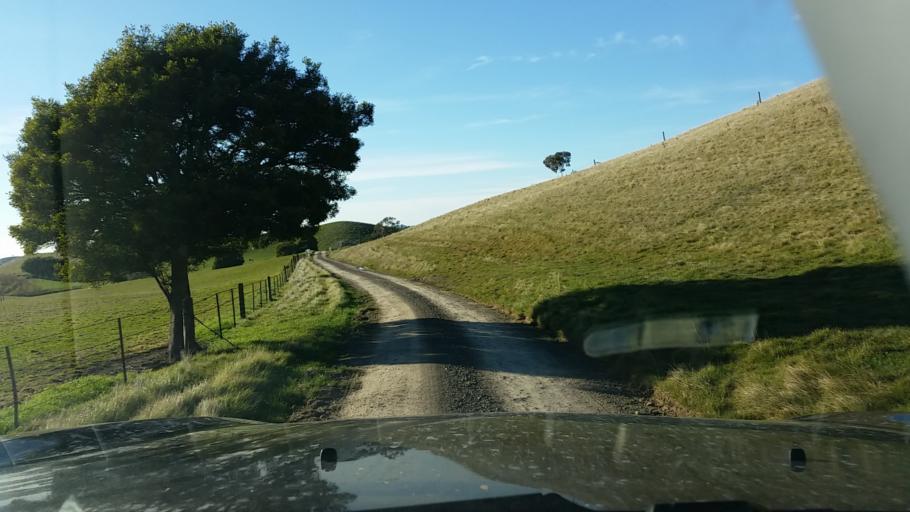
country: NZ
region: Marlborough
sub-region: Marlborough District
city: Blenheim
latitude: -41.7332
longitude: 174.0063
